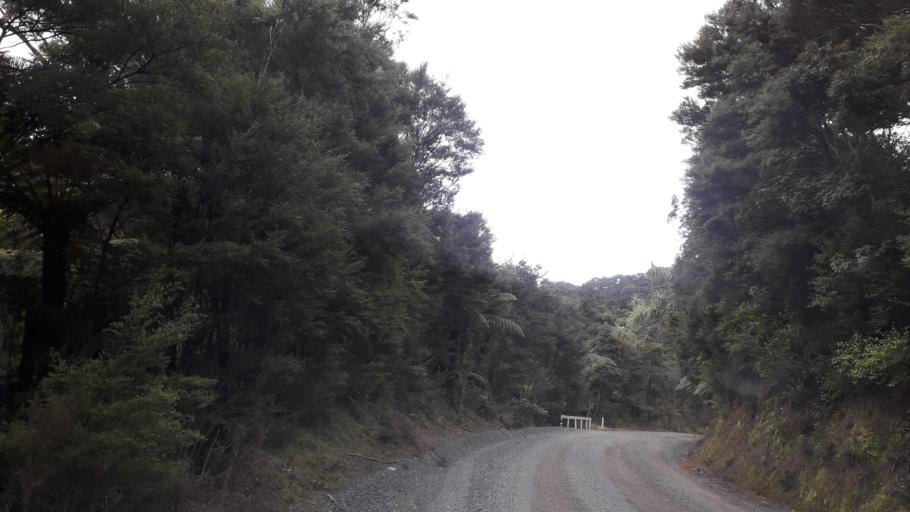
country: NZ
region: Northland
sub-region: Far North District
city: Paihia
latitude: -35.3215
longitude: 174.2340
